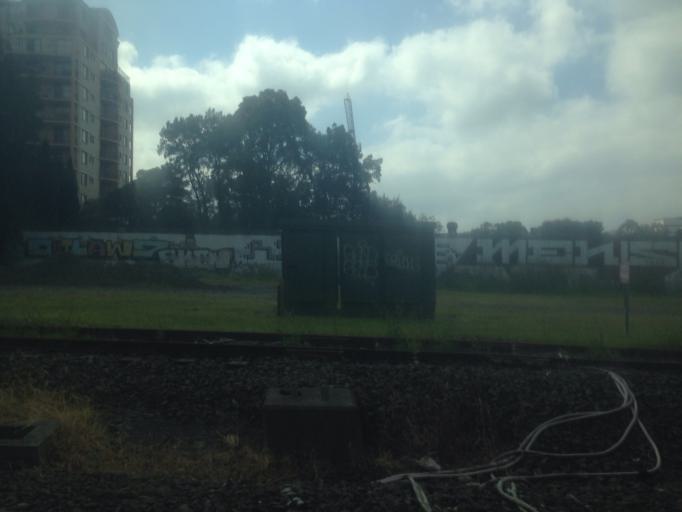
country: AU
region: New South Wales
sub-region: North Sydney
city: St Leonards
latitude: -33.8206
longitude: 151.1939
